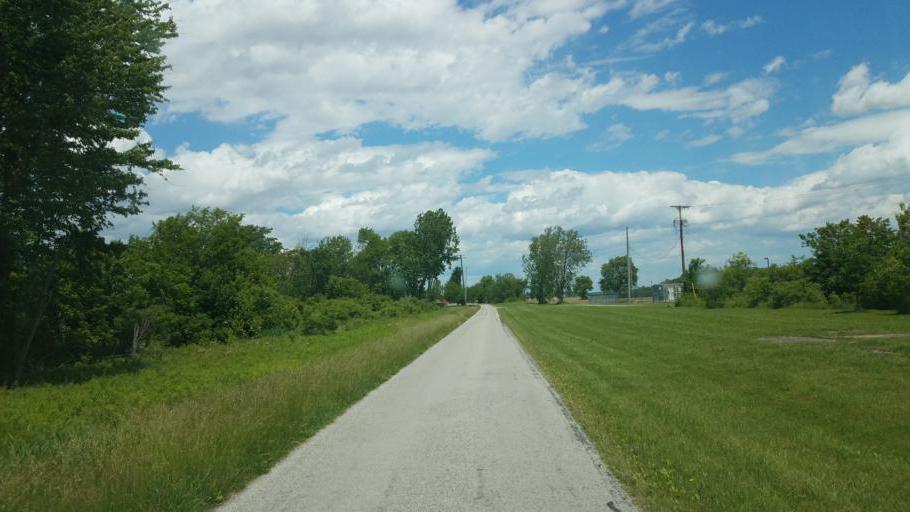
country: US
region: Ohio
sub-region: Huron County
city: Willard
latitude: 41.1386
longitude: -82.7469
